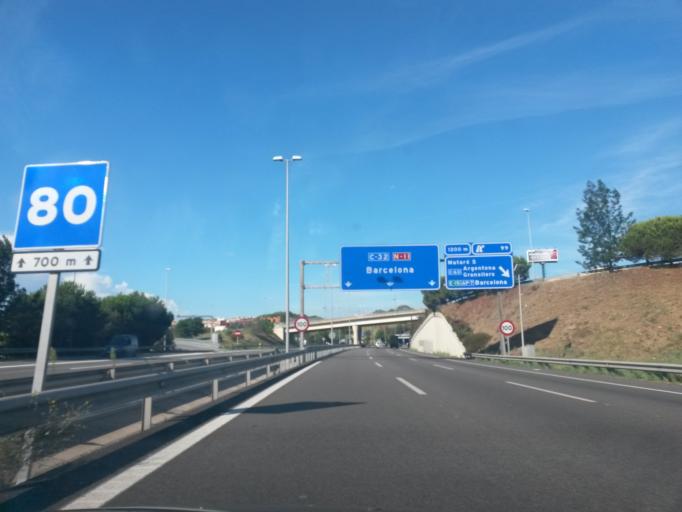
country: ES
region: Catalonia
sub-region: Provincia de Barcelona
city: Mataro
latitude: 41.5529
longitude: 2.4332
